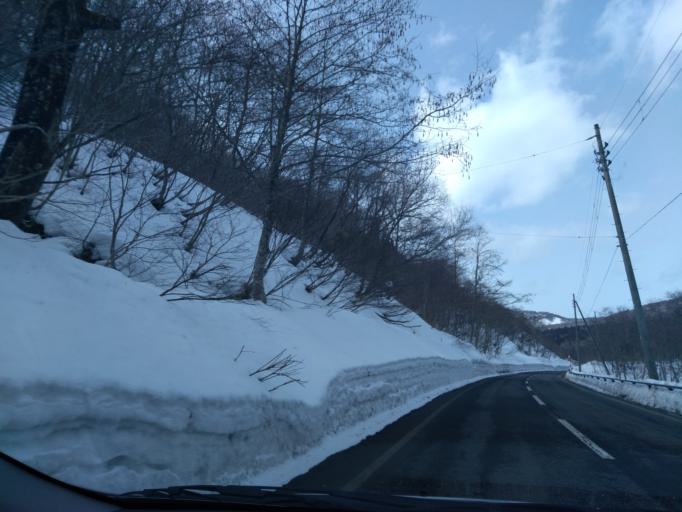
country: JP
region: Iwate
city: Kitakami
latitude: 39.2344
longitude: 140.9276
